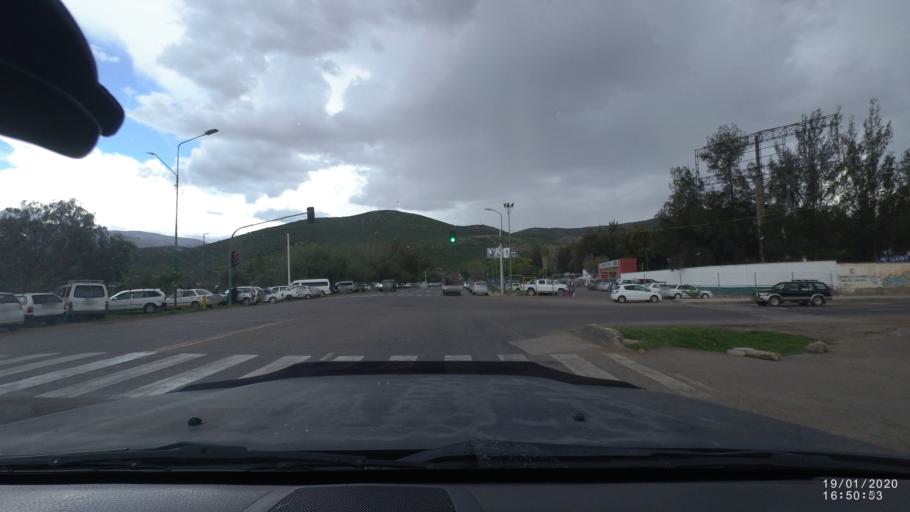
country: BO
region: Cochabamba
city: Cochabamba
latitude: -17.4181
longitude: -66.1317
